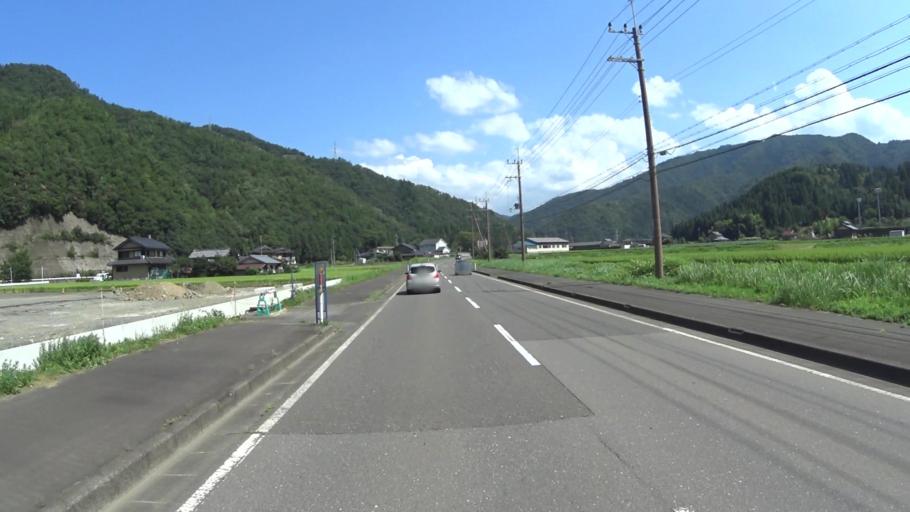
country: JP
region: Fukui
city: Obama
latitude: 35.4087
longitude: 135.6841
